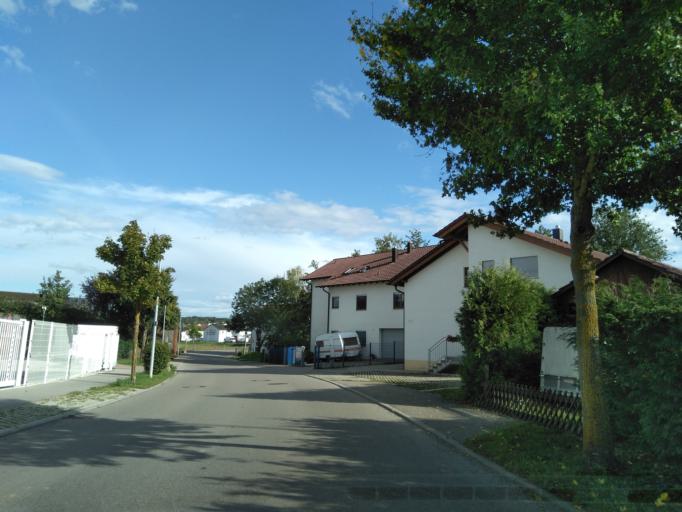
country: DE
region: Baden-Wuerttemberg
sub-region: Regierungsbezirk Stuttgart
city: Sersheim
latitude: 48.9577
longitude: 9.0050
